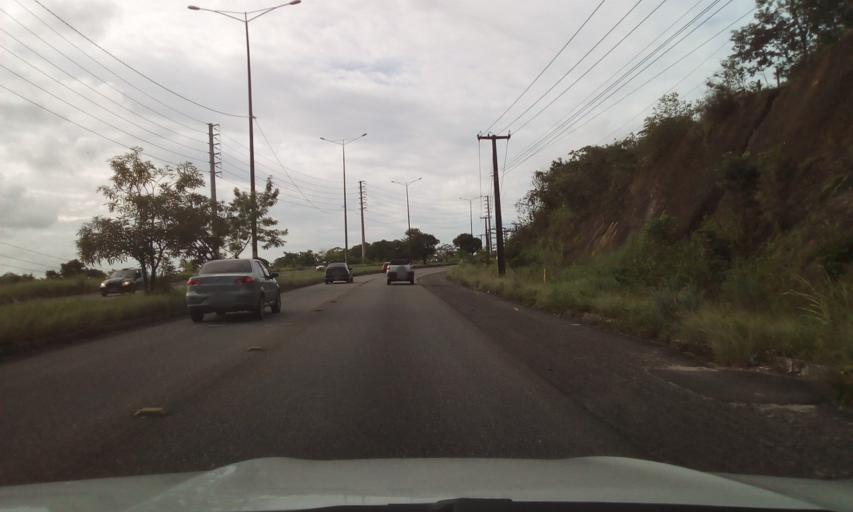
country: BR
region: Paraiba
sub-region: Bayeux
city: Bayeux
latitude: -7.1340
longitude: -34.9051
